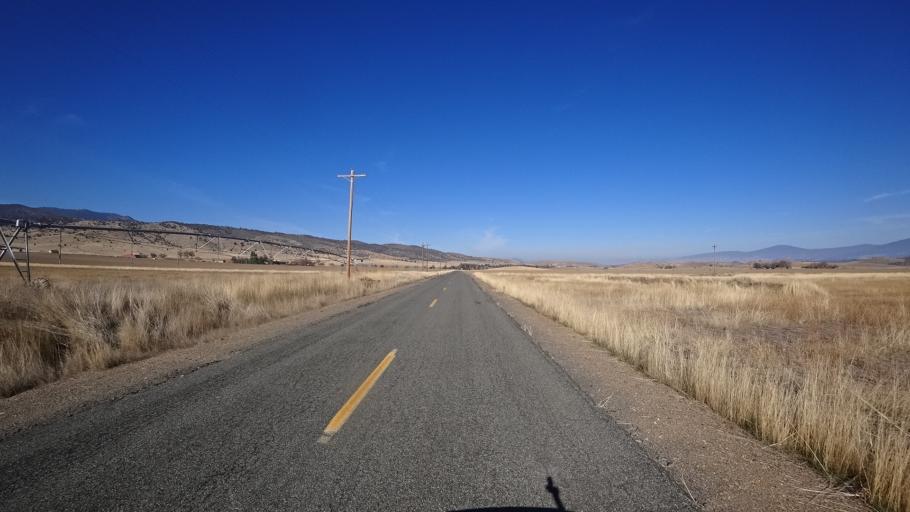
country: US
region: California
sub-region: Siskiyou County
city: Montague
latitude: 41.5671
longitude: -122.5490
